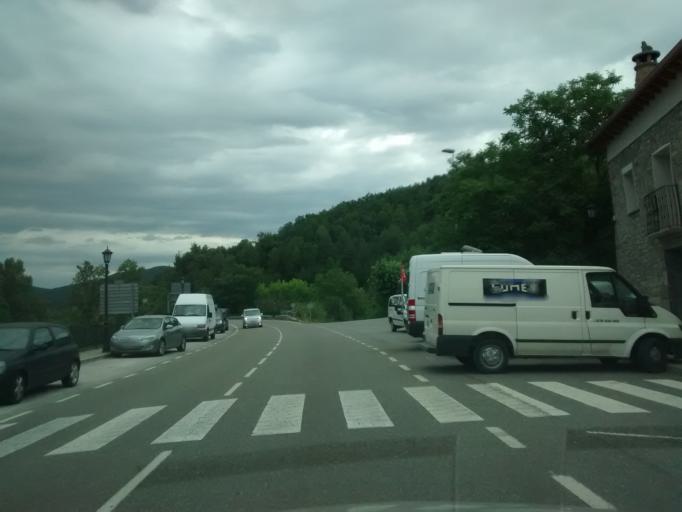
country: ES
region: Aragon
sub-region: Provincia de Huesca
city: Laspuna
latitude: 42.4981
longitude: 0.1441
